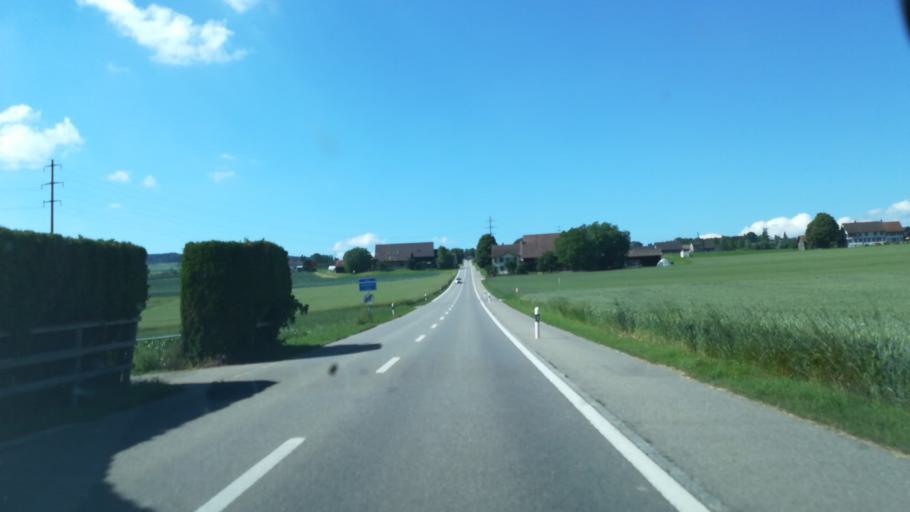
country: CH
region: Thurgau
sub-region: Weinfelden District
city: Berg
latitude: 47.5624
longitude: 9.1730
